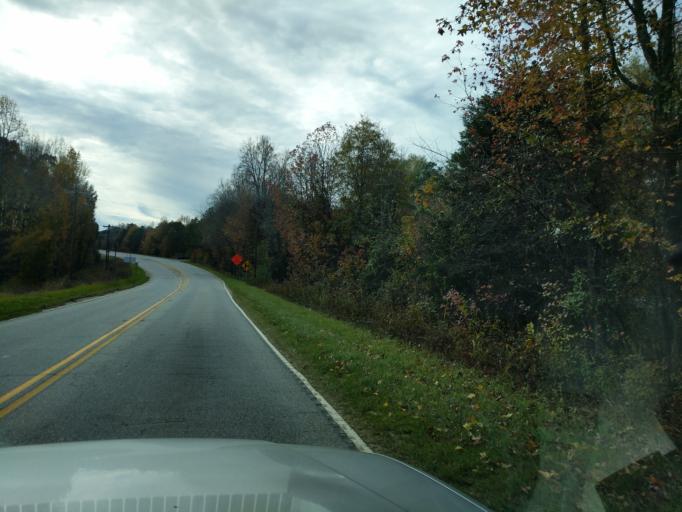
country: US
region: South Carolina
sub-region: Laurens County
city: Watts Mills
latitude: 34.5637
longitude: -82.0066
